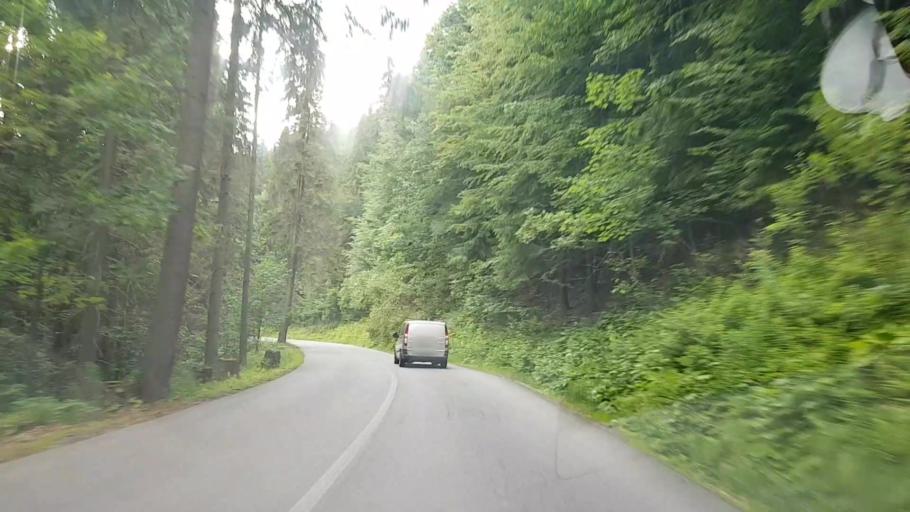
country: RO
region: Harghita
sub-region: Comuna Varsag
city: Varsag
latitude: 46.6724
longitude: 25.3275
